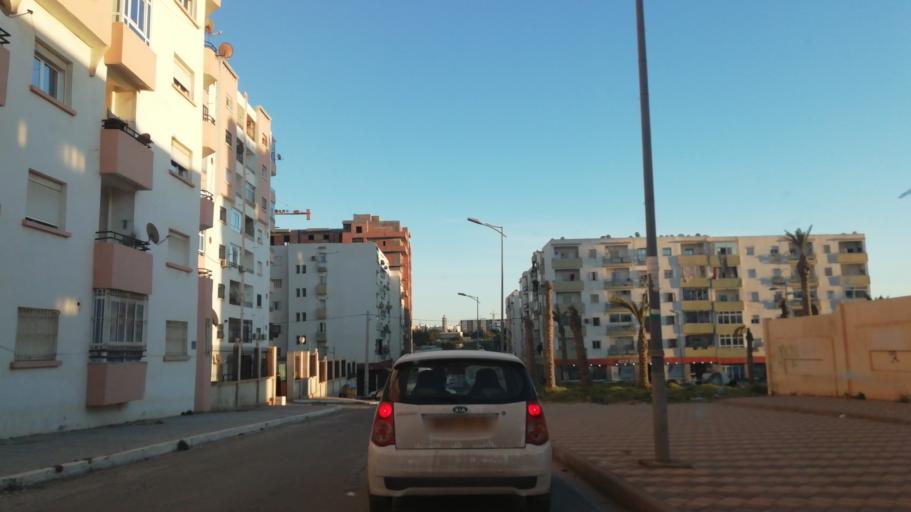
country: DZ
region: Oran
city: Bir el Djir
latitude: 35.7175
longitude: -0.5756
